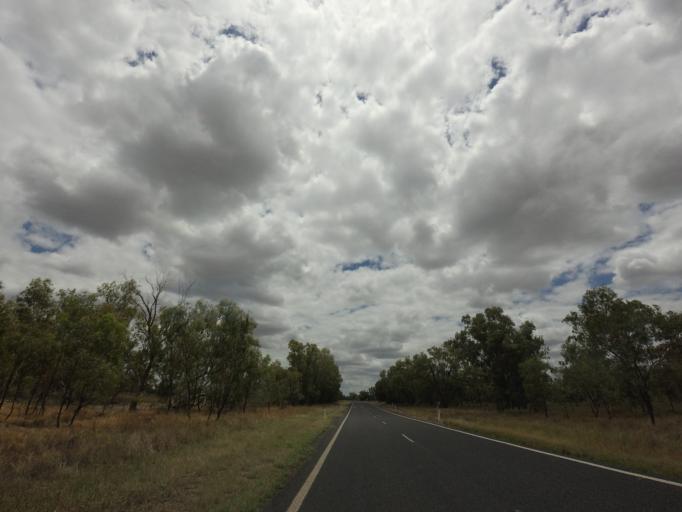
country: AU
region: Queensland
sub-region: Goondiwindi
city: Goondiwindi
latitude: -28.4846
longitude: 150.2935
